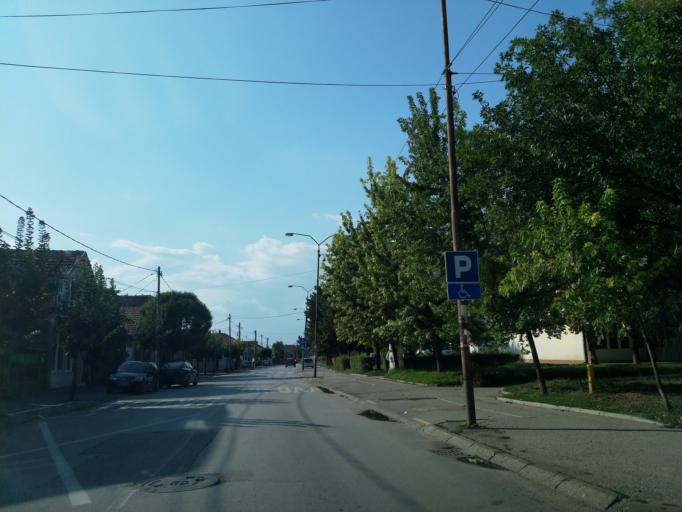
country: RS
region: Central Serbia
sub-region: Pomoravski Okrug
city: Paracin
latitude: 43.8605
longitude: 21.4069
